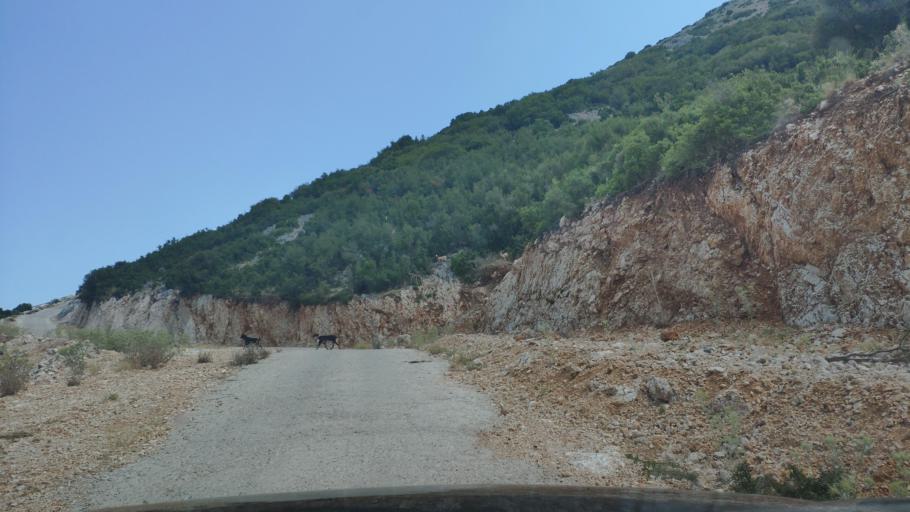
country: GR
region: West Greece
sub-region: Nomos Aitolias kai Akarnanias
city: Monastirakion
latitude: 38.7808
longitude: 20.9761
